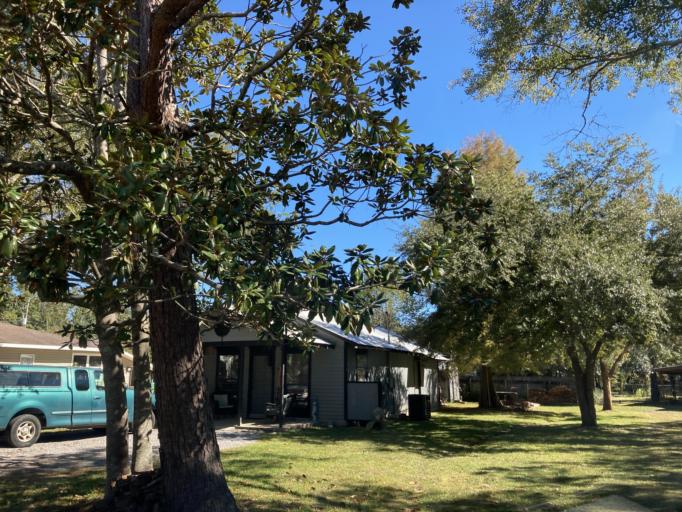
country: US
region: Mississippi
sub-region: Jackson County
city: Ocean Springs
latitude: 30.4107
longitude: -88.8212
